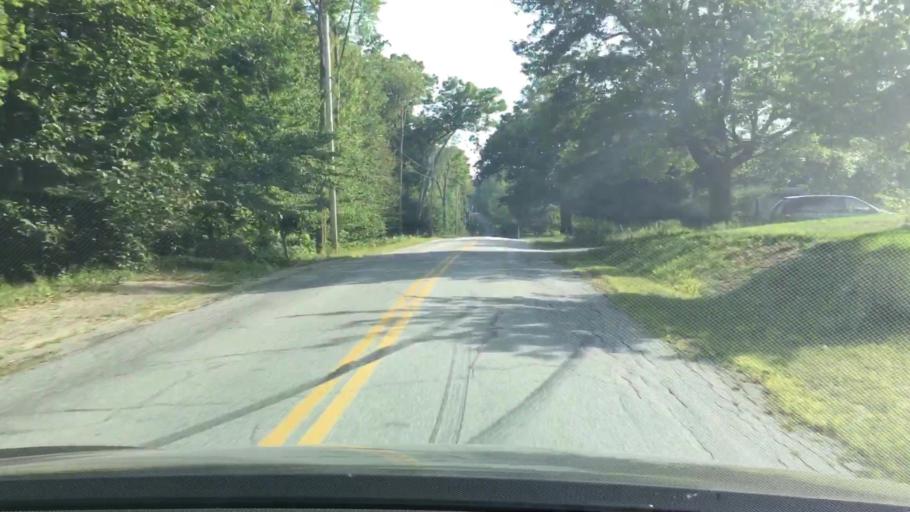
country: US
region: Maine
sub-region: Hancock County
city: Bucksport
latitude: 44.5543
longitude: -68.7953
